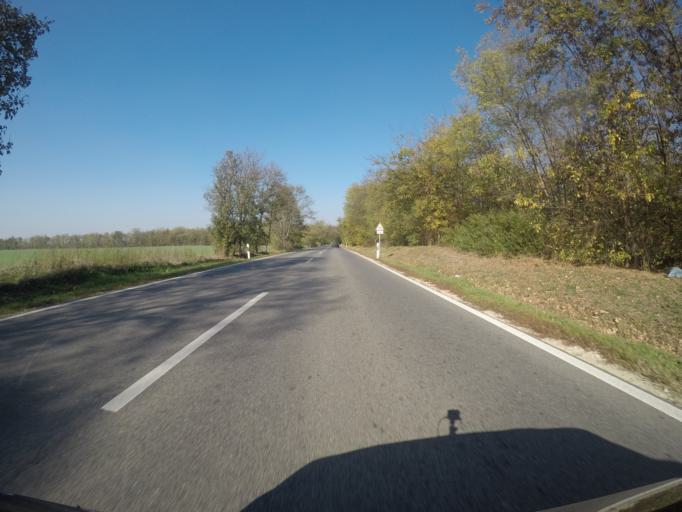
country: HU
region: Tolna
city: Tengelic
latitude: 46.5370
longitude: 18.6539
